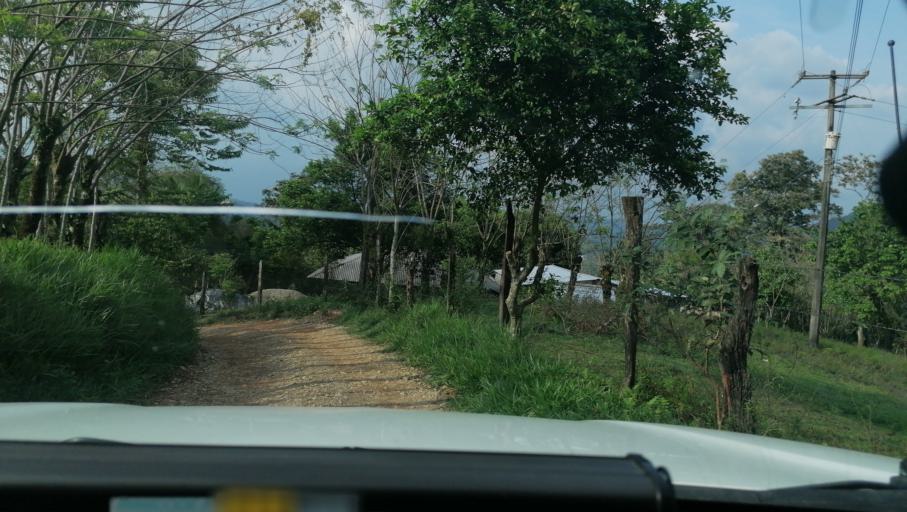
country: MX
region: Chiapas
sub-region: Tapilula
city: San Francisco Jacona
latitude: 17.3271
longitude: -93.0999
